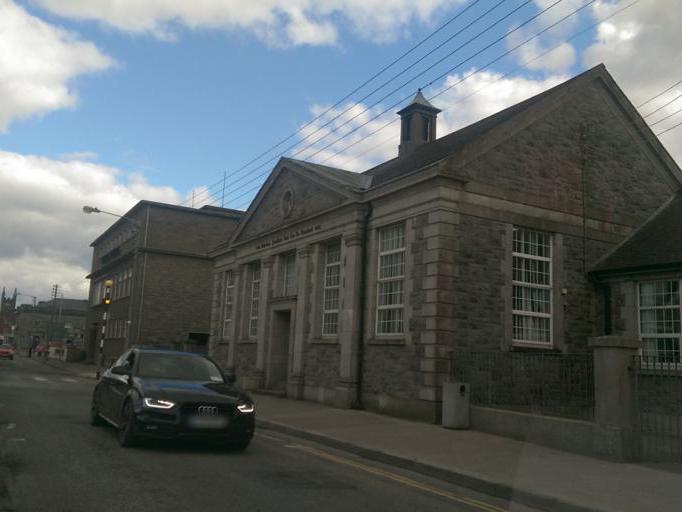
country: IE
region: Connaught
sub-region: County Galway
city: Ballinasloe
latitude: 53.3313
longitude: -8.2273
